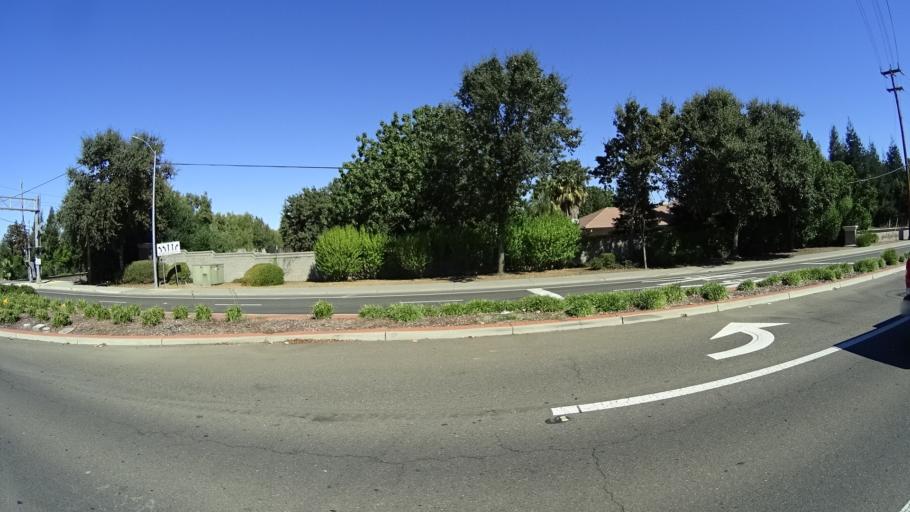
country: US
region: California
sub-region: Sacramento County
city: Elk Grove
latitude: 38.4234
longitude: -121.3695
